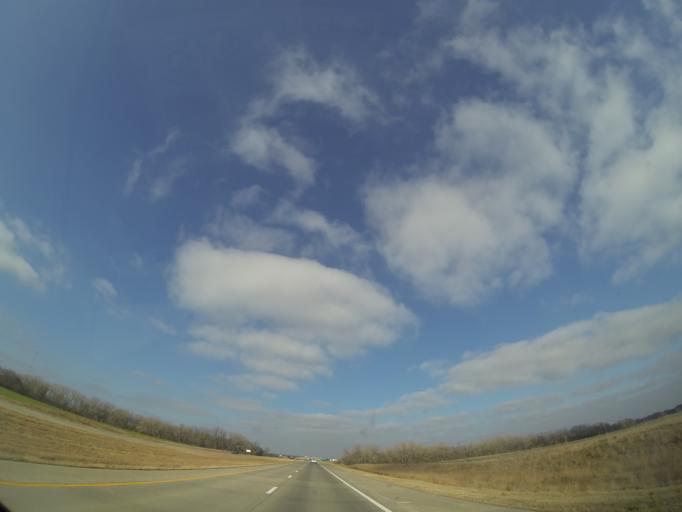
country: US
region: Kansas
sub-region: McPherson County
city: Lindsborg
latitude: 38.6097
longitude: -97.6212
